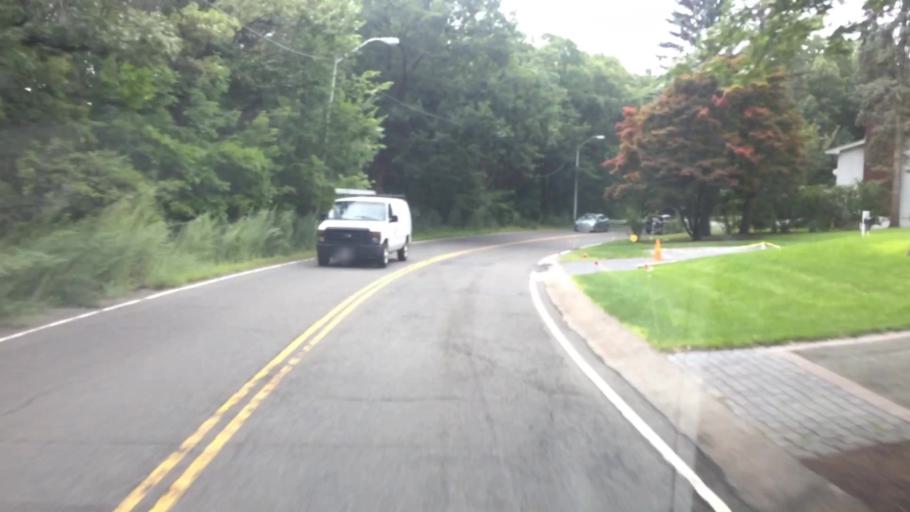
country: US
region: Massachusetts
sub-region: Middlesex County
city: Winchester
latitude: 42.4412
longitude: -71.1229
